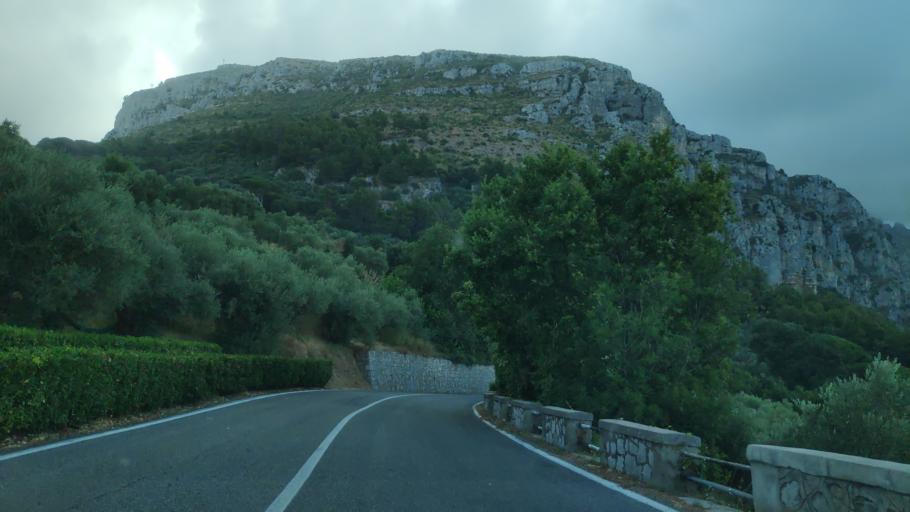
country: IT
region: Campania
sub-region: Provincia di Napoli
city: Arola-Preazzano
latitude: 40.6151
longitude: 14.4332
